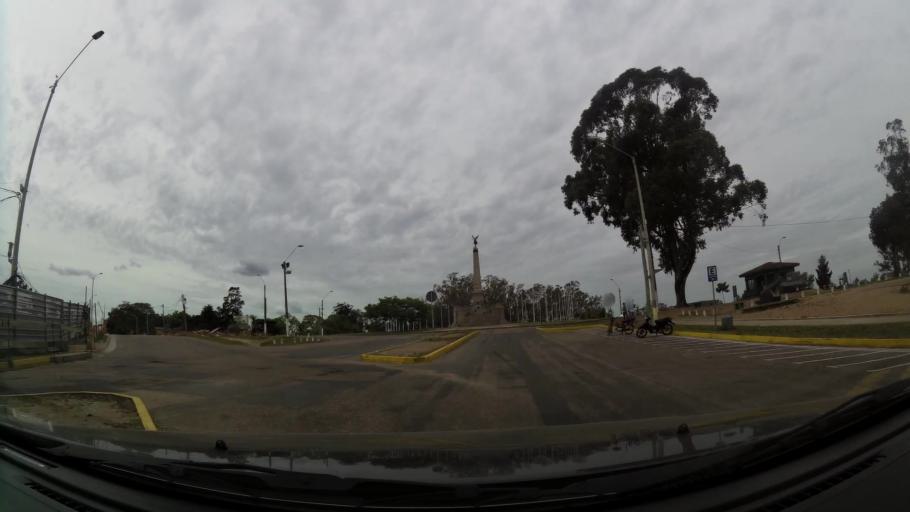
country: UY
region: Canelones
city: Las Piedras
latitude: -34.7258
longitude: -56.2027
